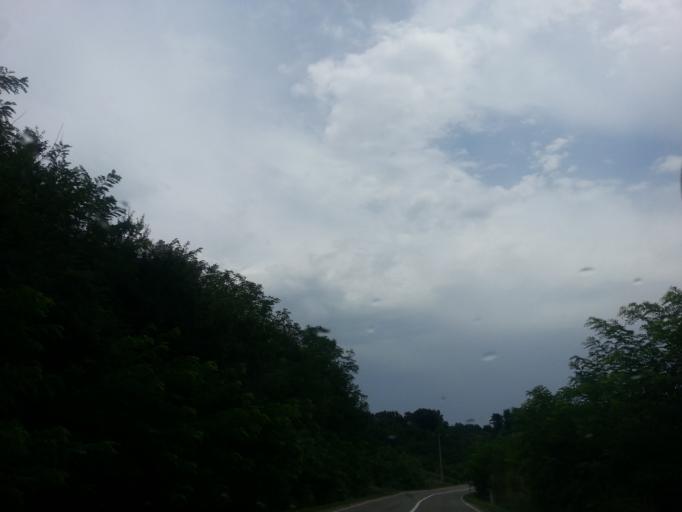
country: BA
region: Republika Srpska
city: Velika Obarska
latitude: 44.7792
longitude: 19.1057
